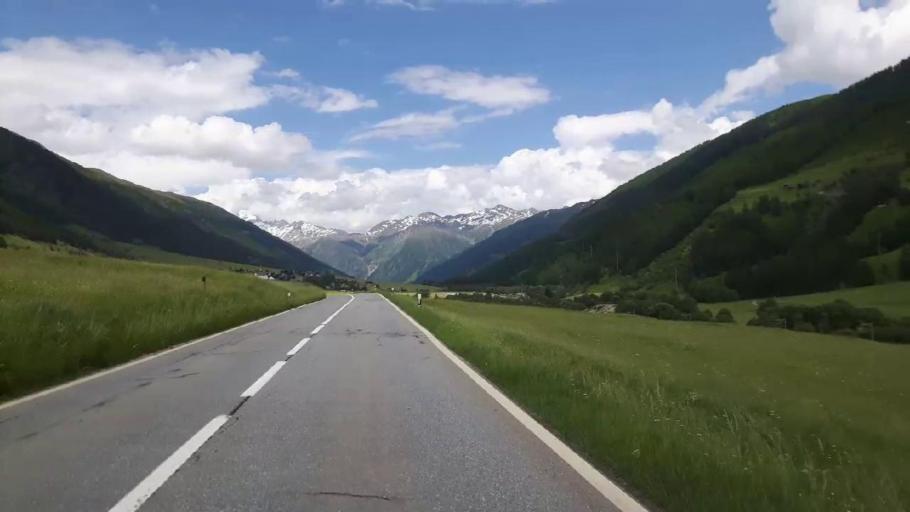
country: CH
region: Valais
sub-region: Goms District
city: Fiesch
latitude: 46.4726
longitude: 8.2471
